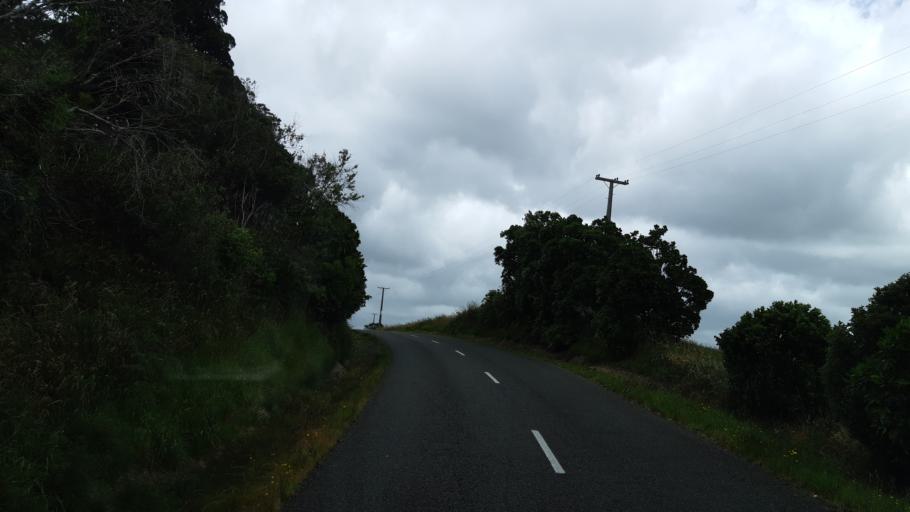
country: NZ
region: Manawatu-Wanganui
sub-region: Palmerston North City
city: Palmerston North
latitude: -39.9373
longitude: 175.9143
